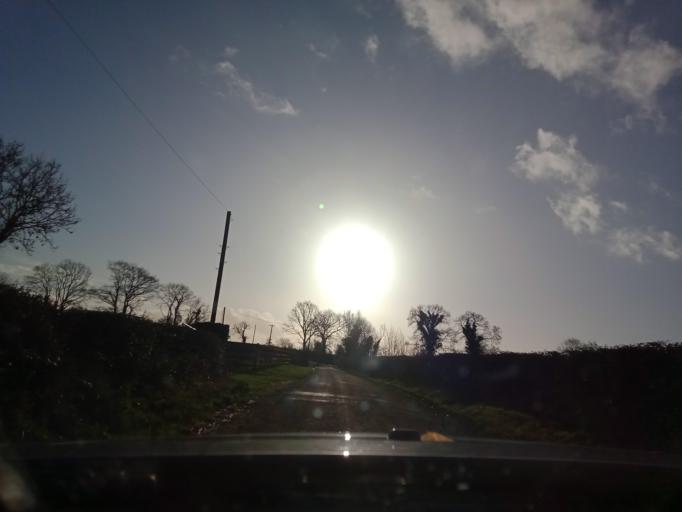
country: IE
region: Leinster
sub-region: Kilkenny
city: Callan
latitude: 52.4951
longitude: -7.3935
